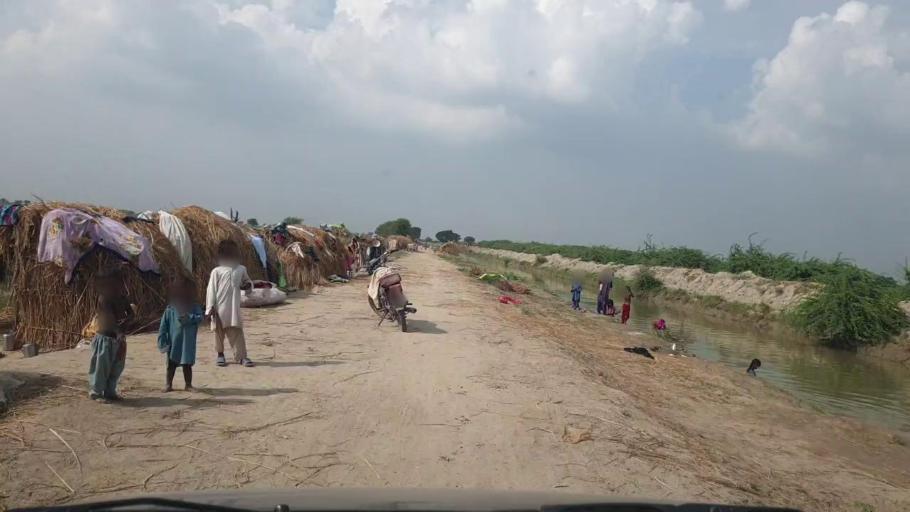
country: PK
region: Sindh
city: Badin
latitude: 24.5724
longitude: 68.6311
